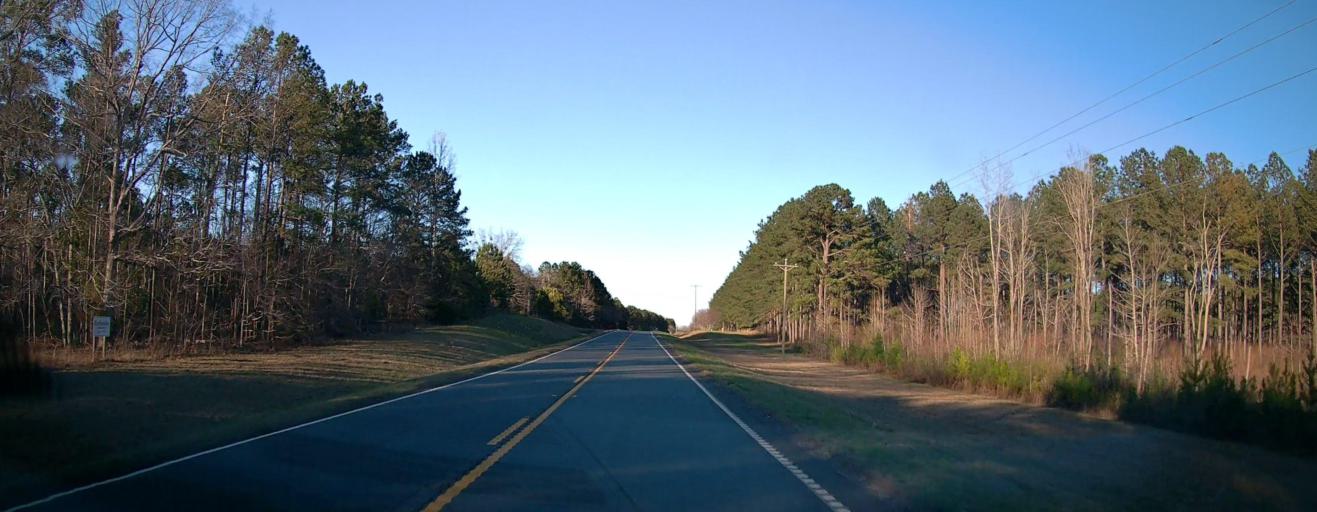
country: US
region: Georgia
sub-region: Talbot County
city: Talbotton
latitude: 32.6181
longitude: -84.5465
